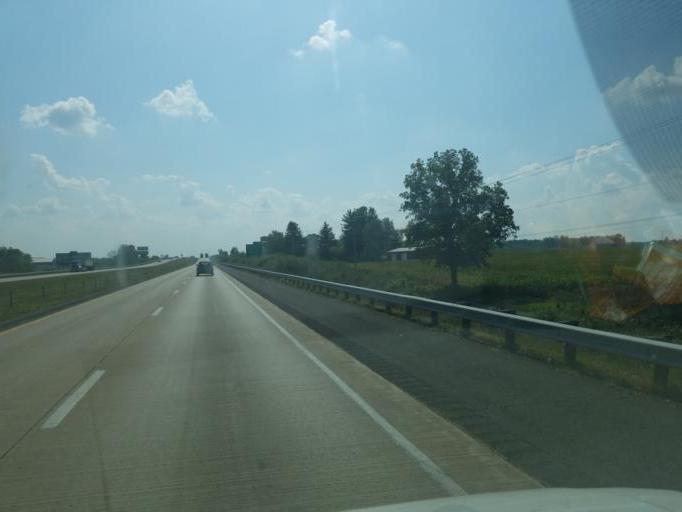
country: US
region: Indiana
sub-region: DeKalb County
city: Auburn
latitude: 41.3418
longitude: -85.0880
